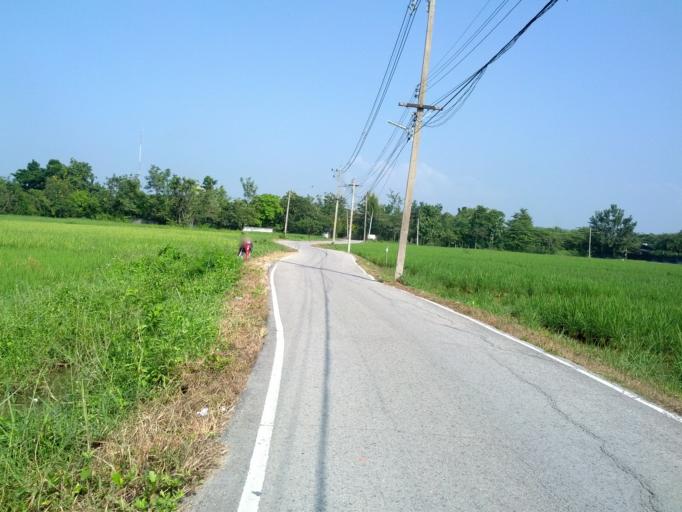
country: TH
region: Chiang Mai
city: San Kamphaeng
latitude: 18.8006
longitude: 99.1018
